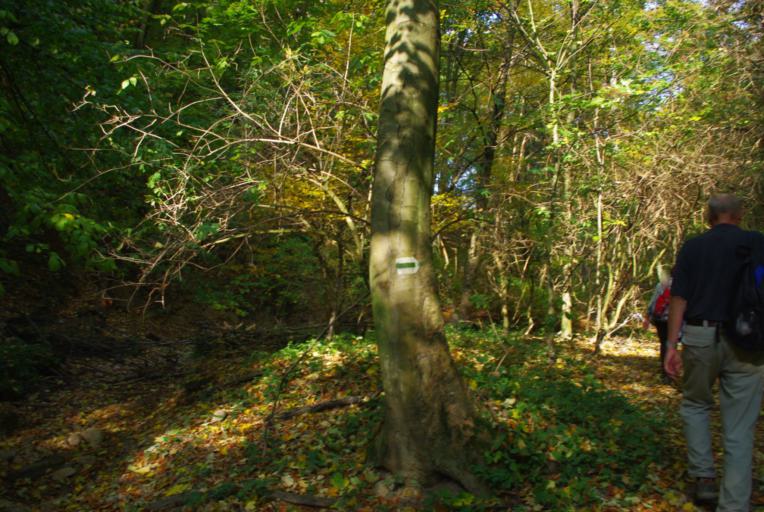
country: HU
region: Veszprem
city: Zirc
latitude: 47.3309
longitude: 17.8907
